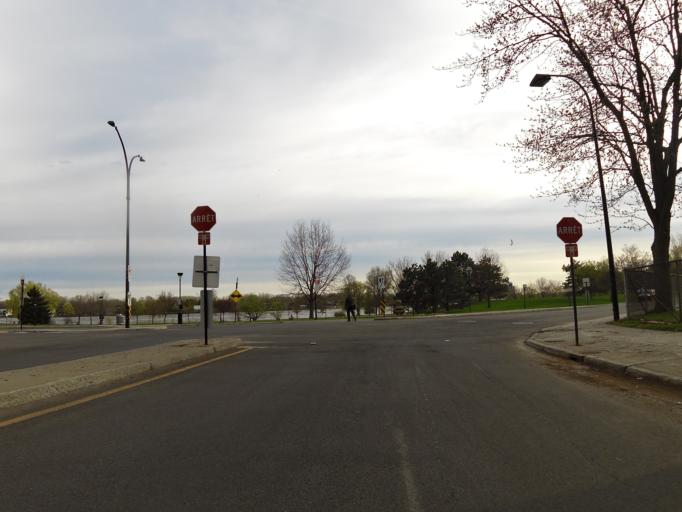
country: CA
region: Quebec
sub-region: Laval
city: Laval
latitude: 45.5458
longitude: -73.6923
